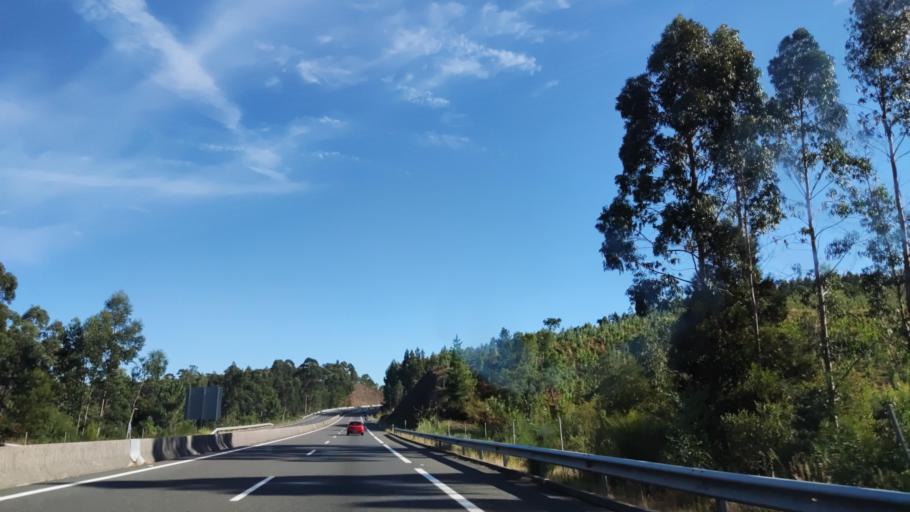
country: ES
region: Galicia
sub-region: Provincia da Coruna
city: Boiro
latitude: 42.5986
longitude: -8.9696
